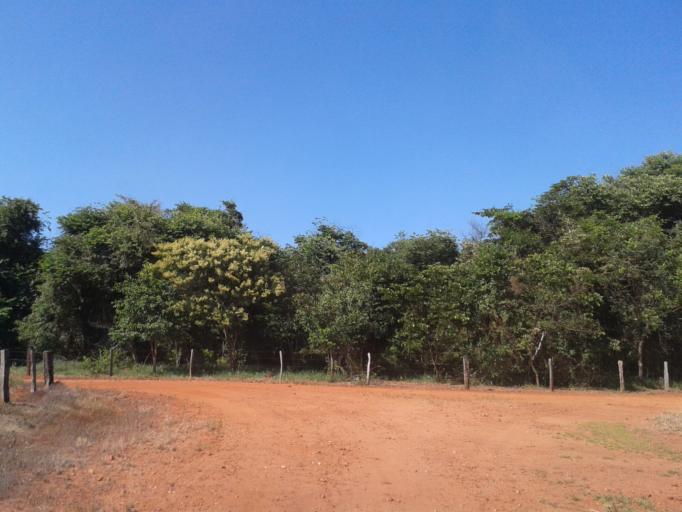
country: BR
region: Minas Gerais
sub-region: Santa Vitoria
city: Santa Vitoria
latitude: -19.1191
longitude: -50.4882
